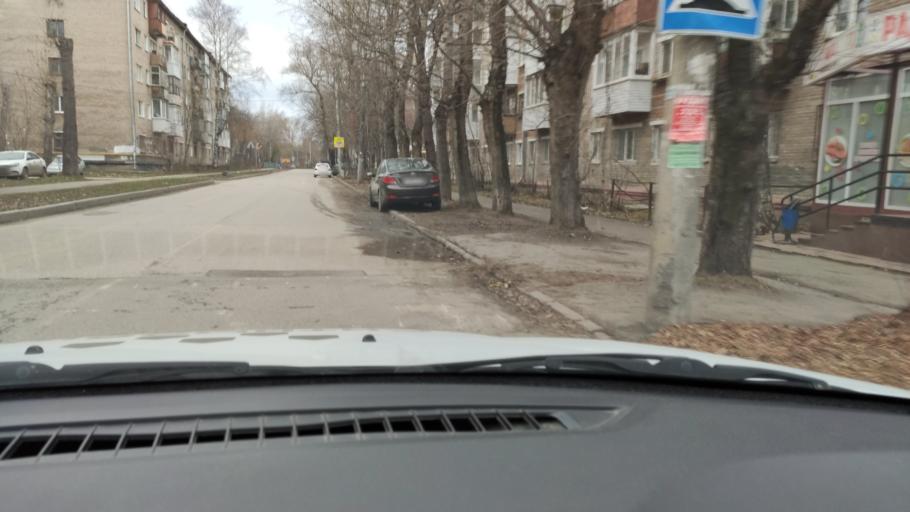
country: RU
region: Perm
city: Perm
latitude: 58.0139
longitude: 56.2899
